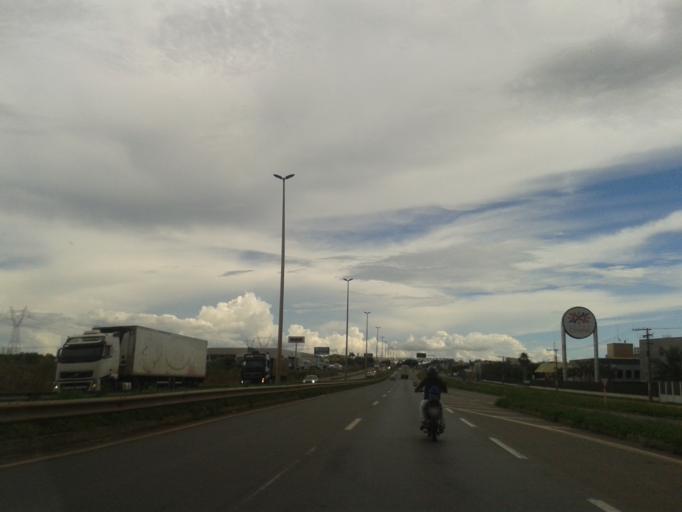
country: BR
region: Goias
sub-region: Aparecida De Goiania
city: Aparecida de Goiania
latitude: -16.8058
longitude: -49.2393
